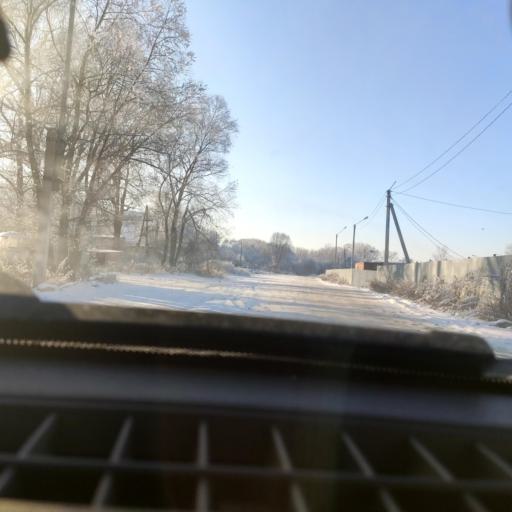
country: RU
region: Bashkortostan
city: Ufa
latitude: 54.8307
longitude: 56.0569
